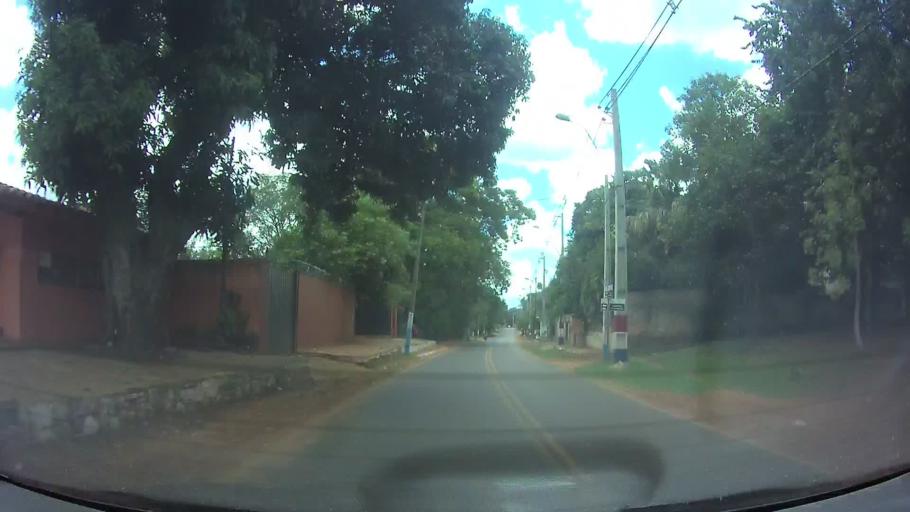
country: PY
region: Central
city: Capiata
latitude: -25.2981
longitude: -57.4416
